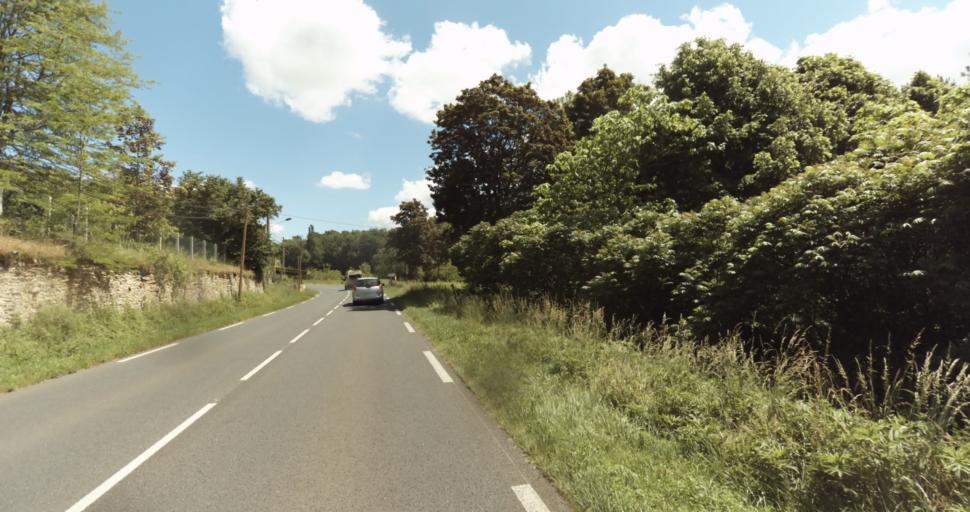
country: FR
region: Aquitaine
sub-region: Departement de la Dordogne
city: Le Bugue
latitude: 44.8403
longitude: 0.8582
